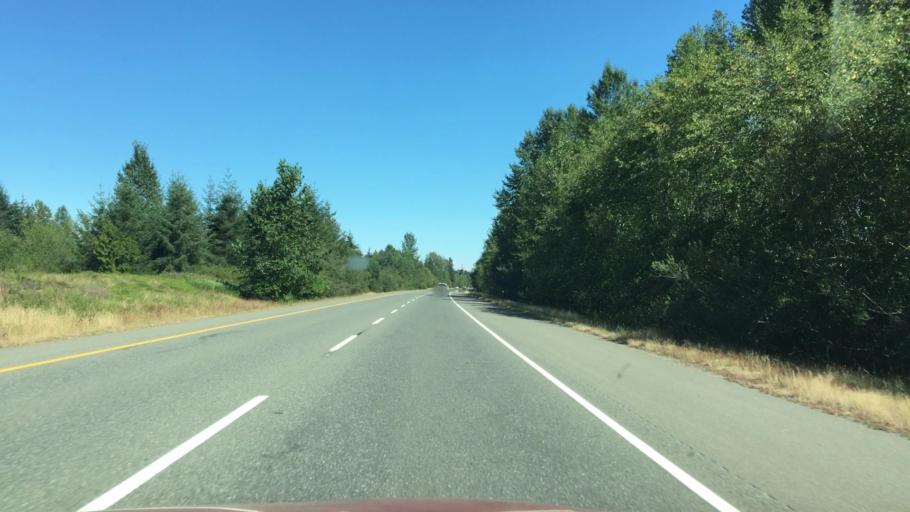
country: CA
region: British Columbia
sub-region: Regional District of Nanaimo
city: Parksville
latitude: 49.3163
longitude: -124.3735
